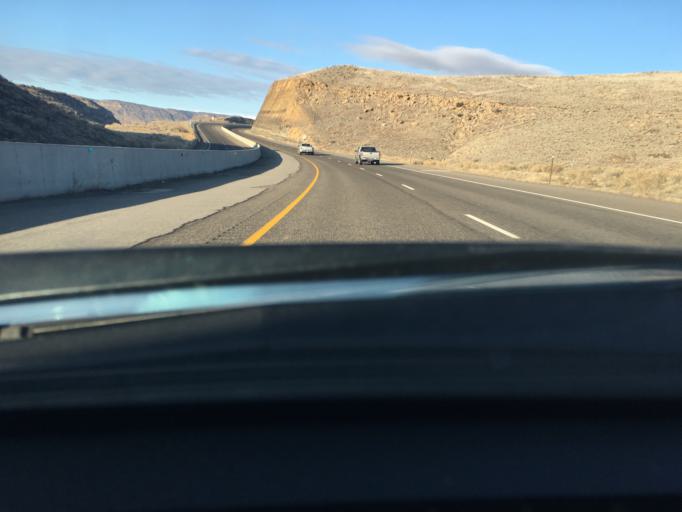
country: US
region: Colorado
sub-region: Delta County
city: Delta
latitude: 38.8118
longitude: -108.2845
